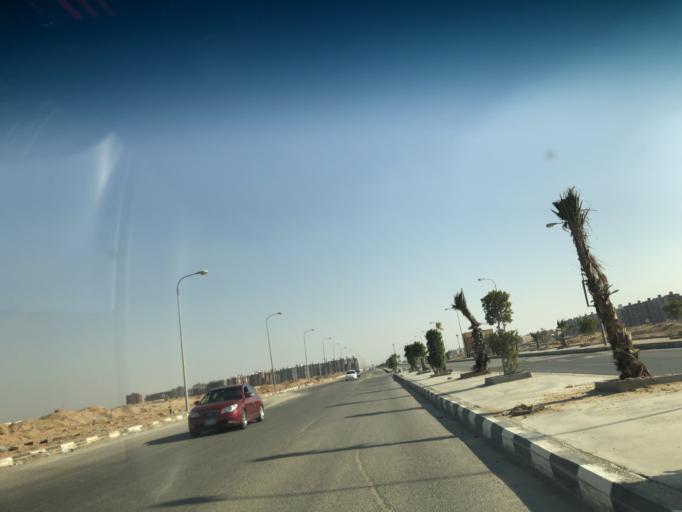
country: EG
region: Al Jizah
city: Madinat Sittah Uktubar
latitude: 29.9118
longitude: 31.0702
